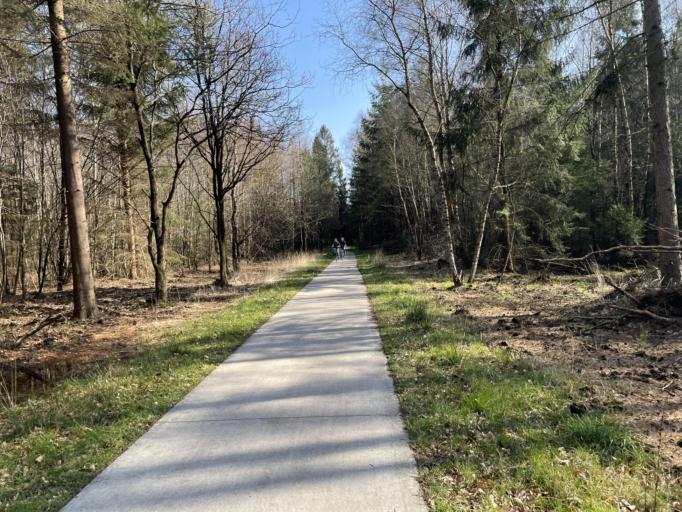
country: NL
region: Drenthe
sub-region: Gemeente Westerveld
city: Dwingeloo
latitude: 52.9120
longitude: 6.3490
